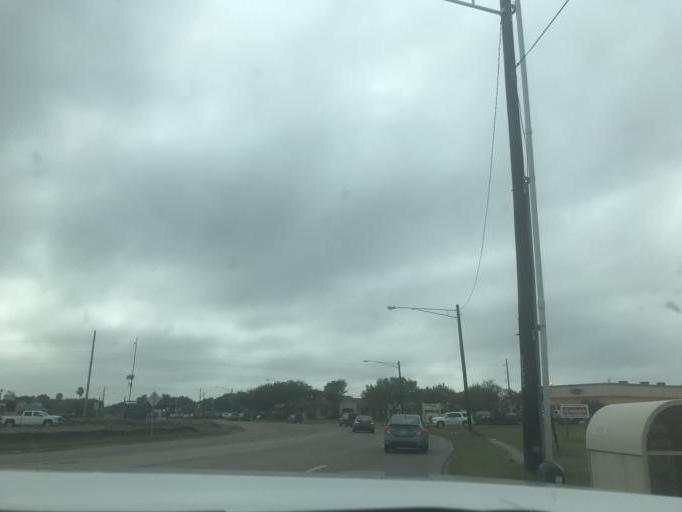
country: US
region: Texas
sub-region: Nueces County
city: Corpus Christi
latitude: 27.6864
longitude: -97.3642
